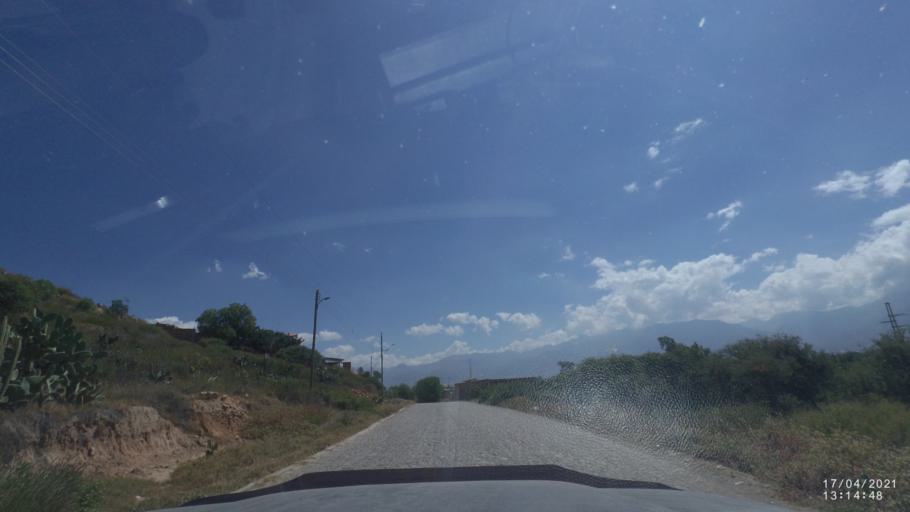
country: BO
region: Cochabamba
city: Cochabamba
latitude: -17.4168
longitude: -66.2273
